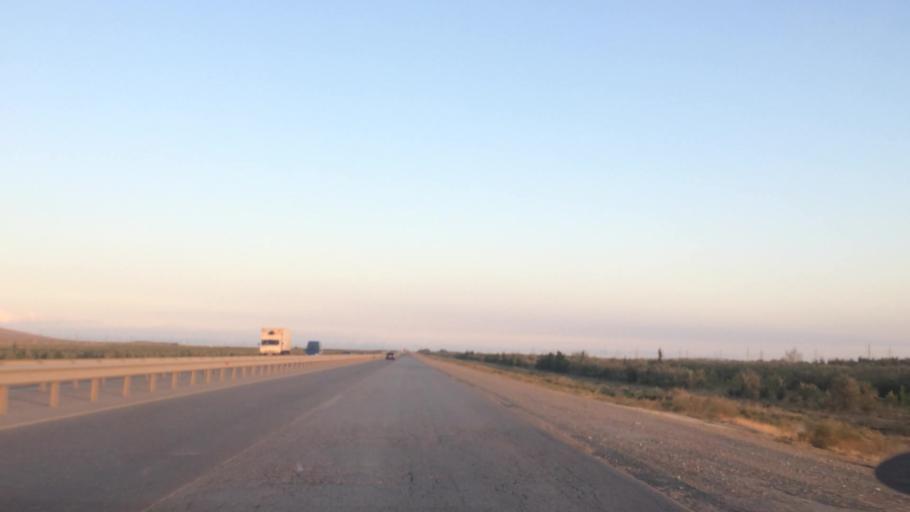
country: AZ
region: Baki
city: Qobustan
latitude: 39.9609
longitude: 49.2927
